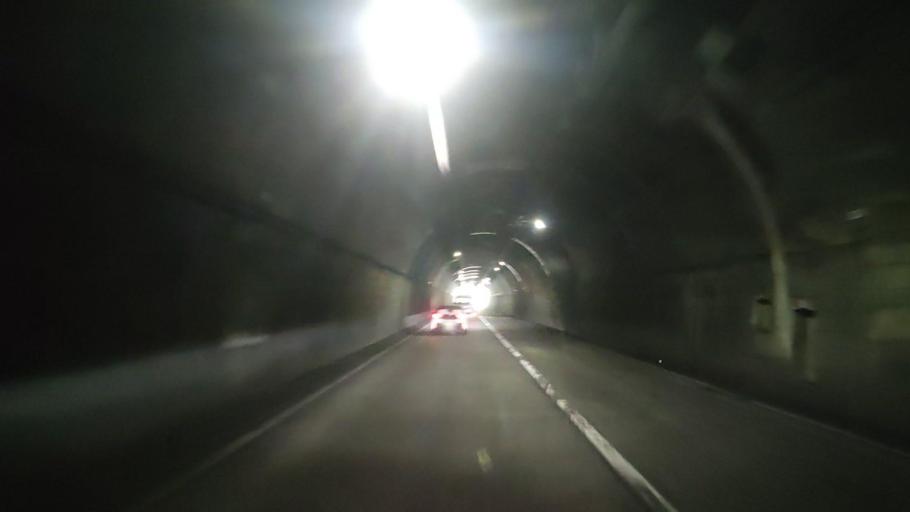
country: JP
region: Mie
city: Owase
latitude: 34.1553
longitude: 136.2647
